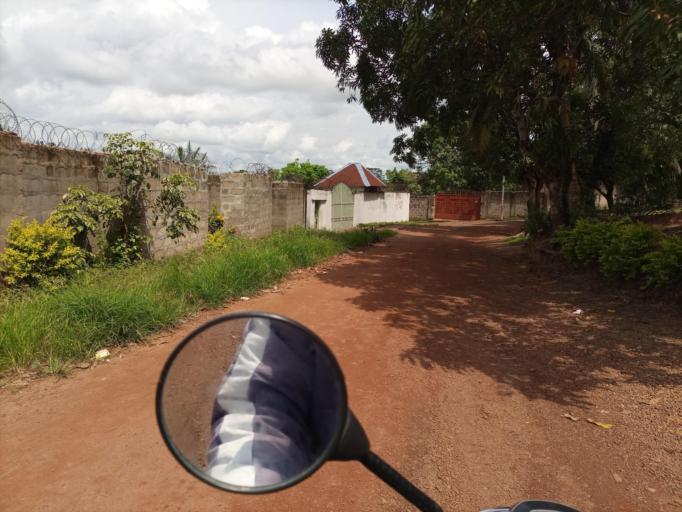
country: SL
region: Southern Province
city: Bo
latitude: 7.9717
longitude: -11.7623
